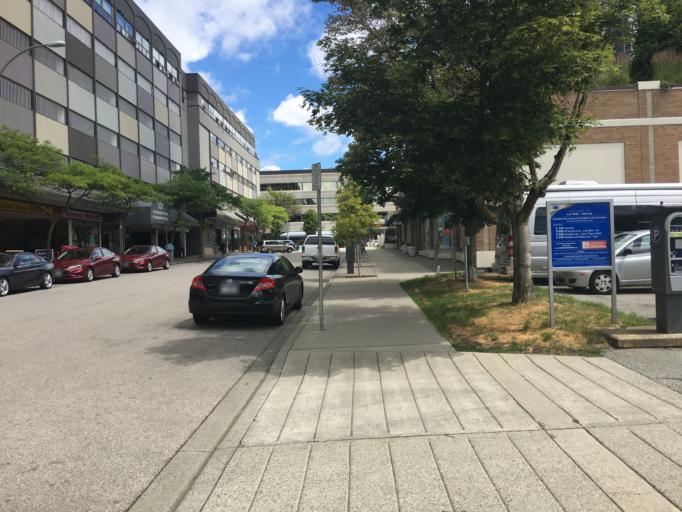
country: CA
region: British Columbia
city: New Westminster
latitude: 49.2118
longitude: -122.9206
